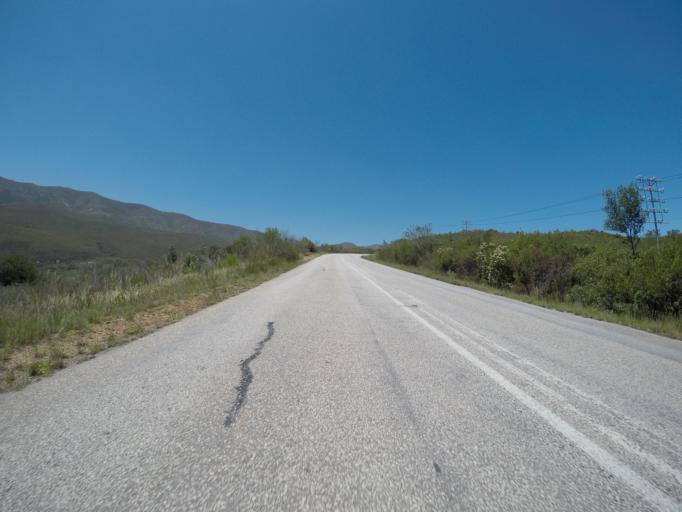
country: ZA
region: Eastern Cape
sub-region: Cacadu District Municipality
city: Kareedouw
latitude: -33.8862
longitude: 24.0794
